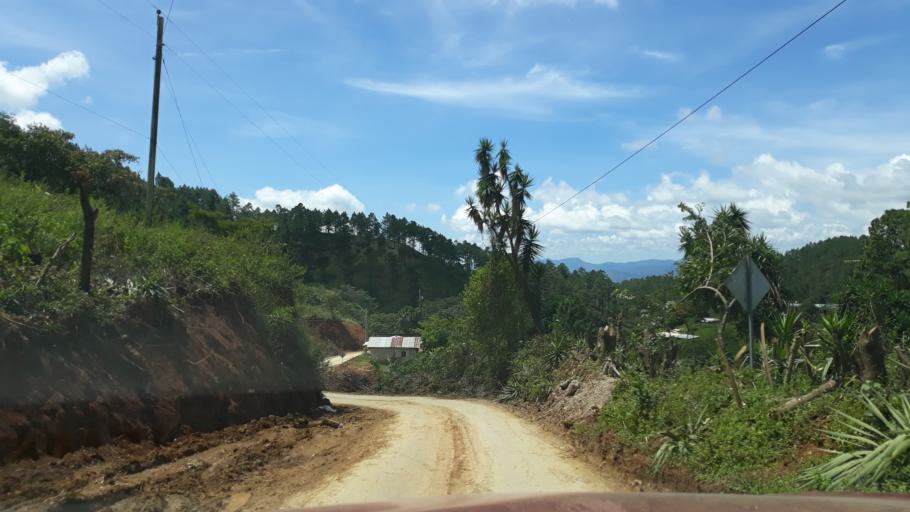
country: HN
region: El Paraiso
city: Santa Cruz
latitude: 13.7548
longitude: -86.6562
